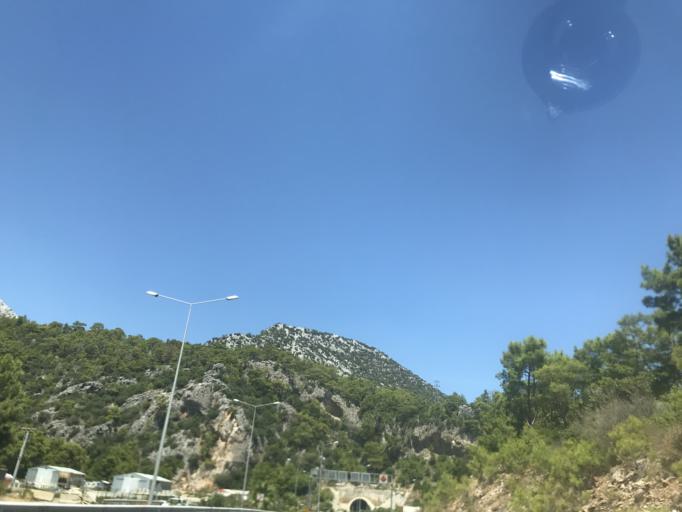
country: TR
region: Antalya
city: Cakirlar
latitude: 36.7597
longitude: 30.5697
